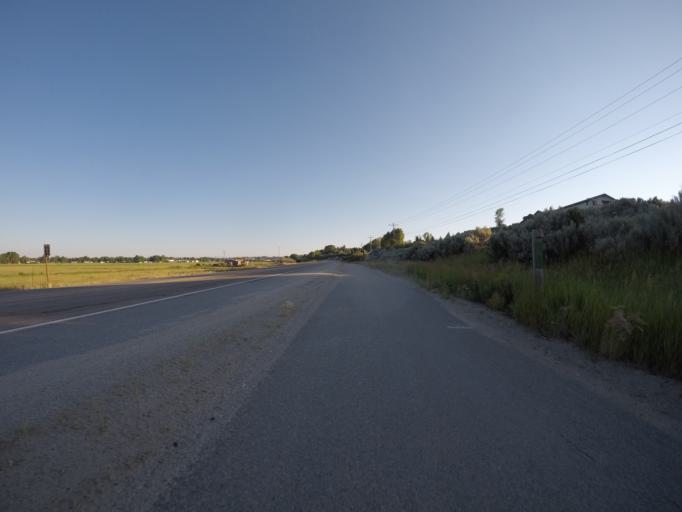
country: US
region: Wyoming
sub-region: Sublette County
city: Pinedale
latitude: 42.8571
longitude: -109.8503
